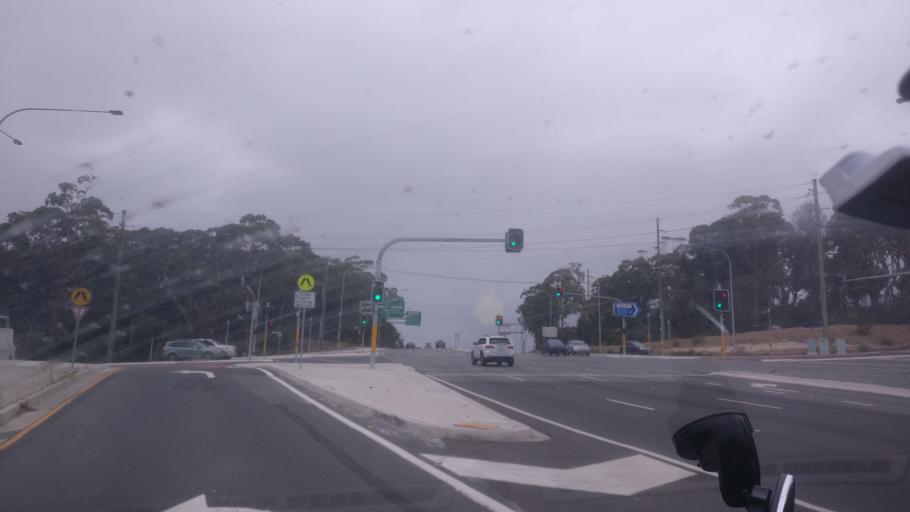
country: AU
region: New South Wales
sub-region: Warringah
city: Allambie Heights
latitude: -33.7495
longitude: 151.2351
